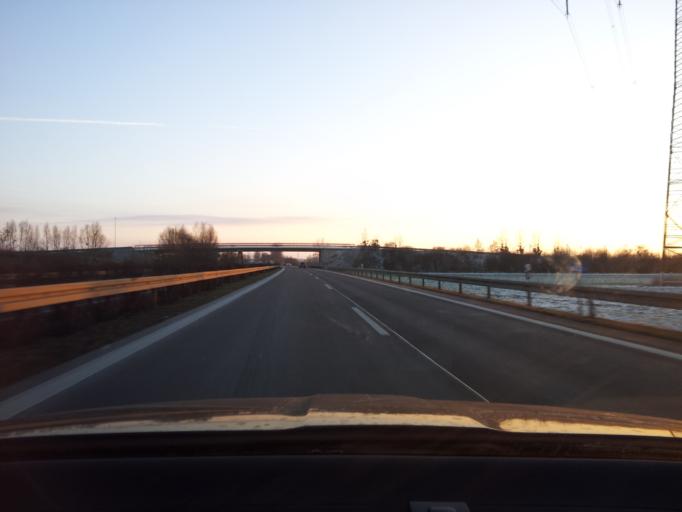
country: DE
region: Brandenburg
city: Brieselang
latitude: 52.6050
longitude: 12.9704
